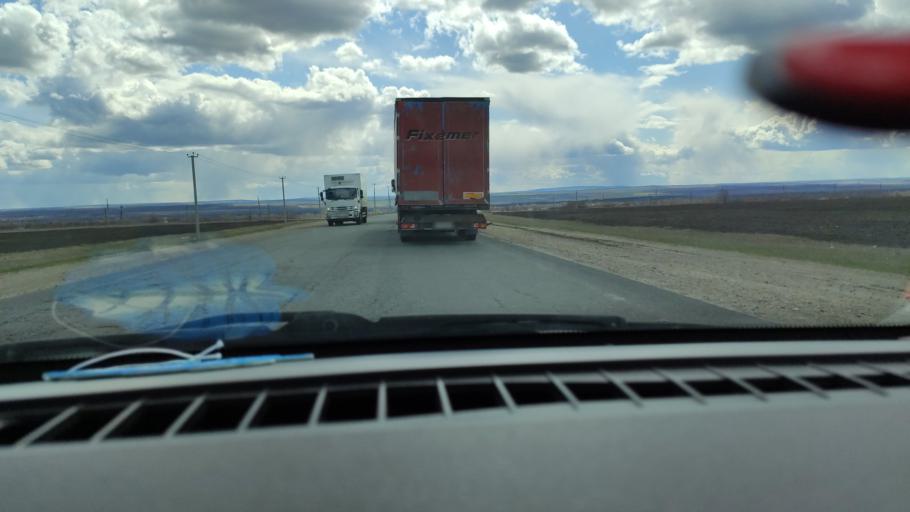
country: RU
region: Samara
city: Varlamovo
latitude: 53.1823
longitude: 48.2881
